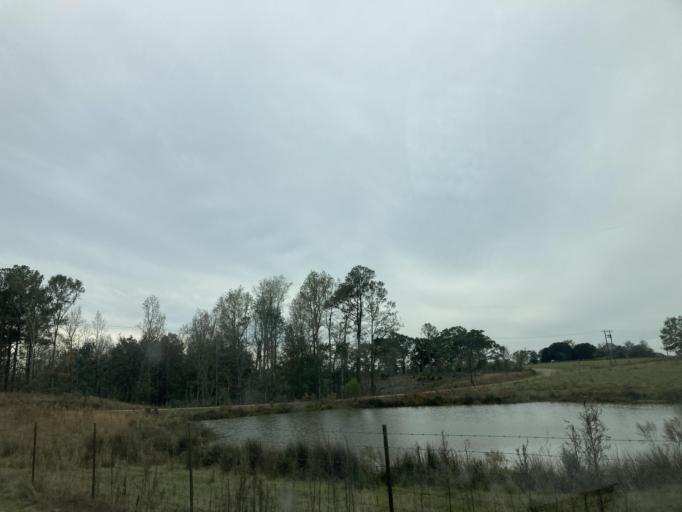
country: US
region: Mississippi
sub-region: Lamar County
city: Lumberton
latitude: 31.0437
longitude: -89.4506
